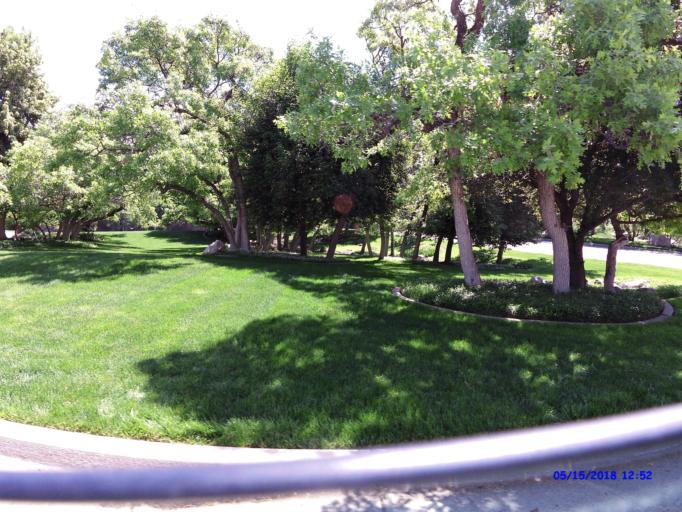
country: US
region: Utah
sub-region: Weber County
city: Uintah
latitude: 41.1591
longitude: -111.9228
